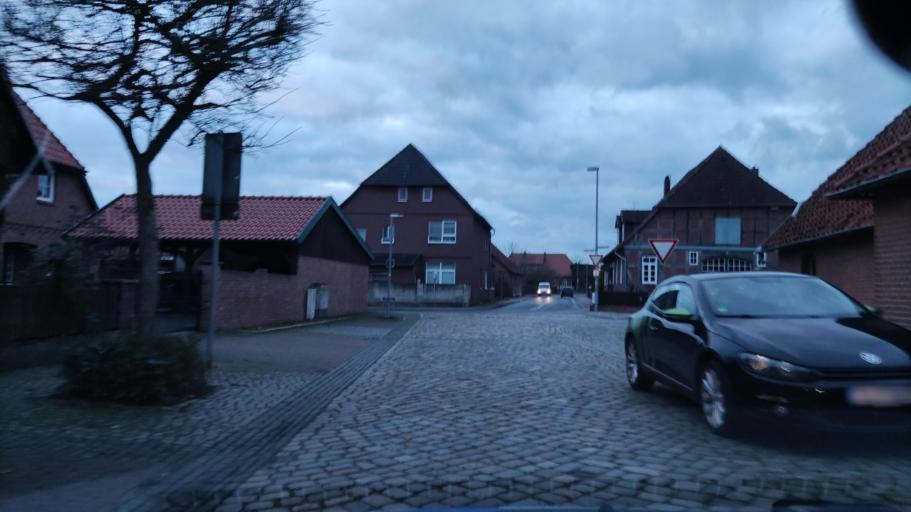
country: DE
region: Lower Saxony
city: Schwarmstedt
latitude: 52.5995
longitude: 9.5689
